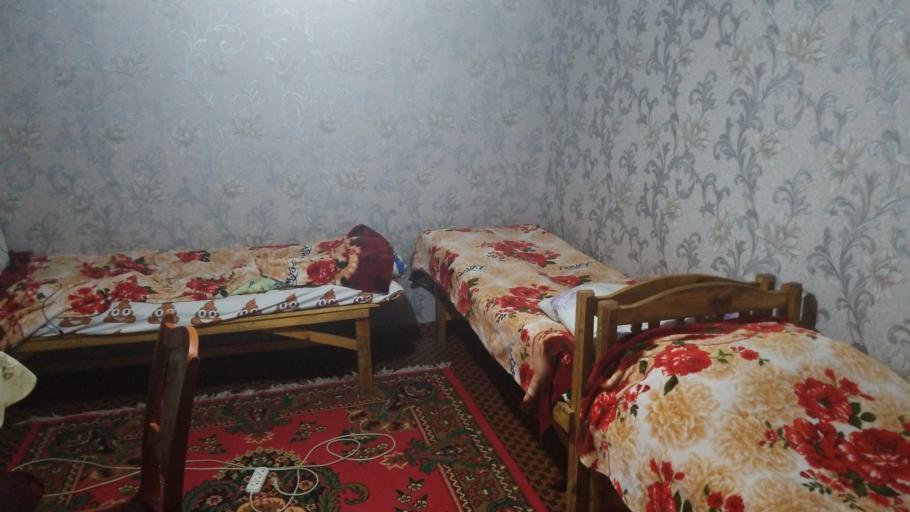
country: TJ
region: Gorno-Badakhshan
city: Murghob
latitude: 38.1778
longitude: 73.9722
